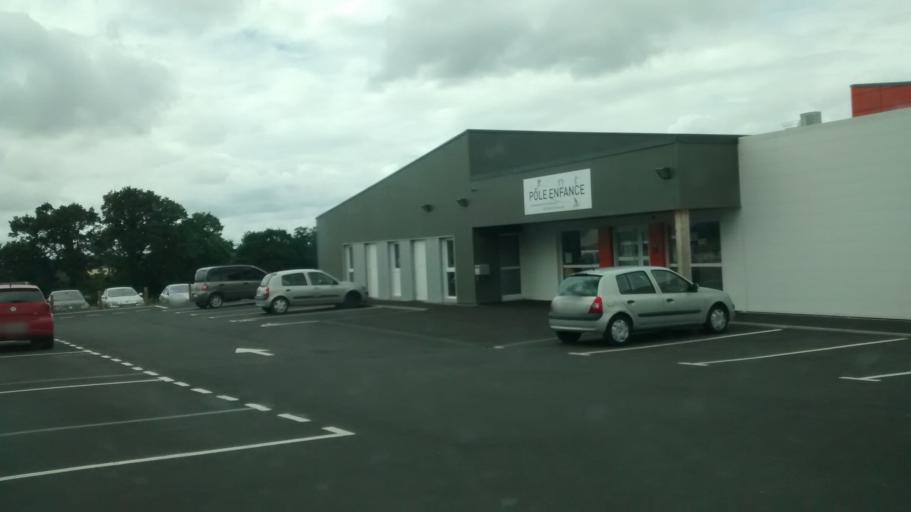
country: FR
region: Brittany
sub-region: Departement du Morbihan
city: Carentoir
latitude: 47.8196
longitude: -2.1358
